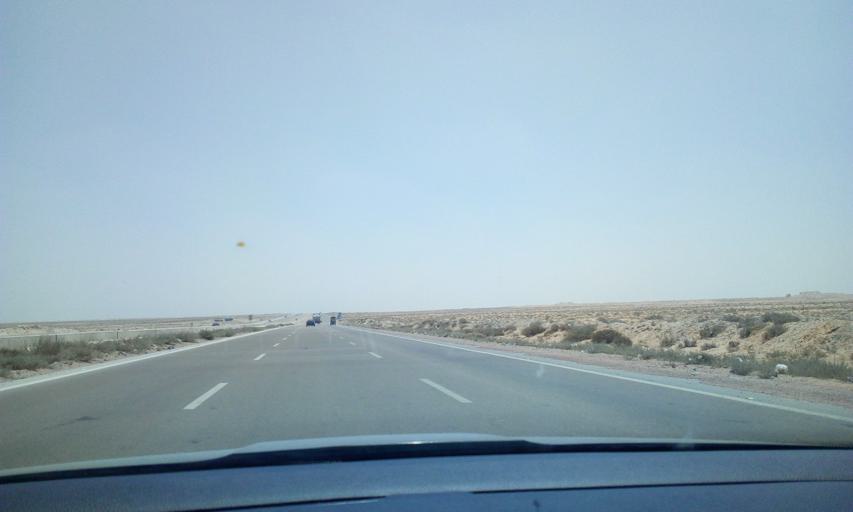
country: EG
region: Al Buhayrah
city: Abu al Matamir
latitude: 30.6140
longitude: 29.8140
